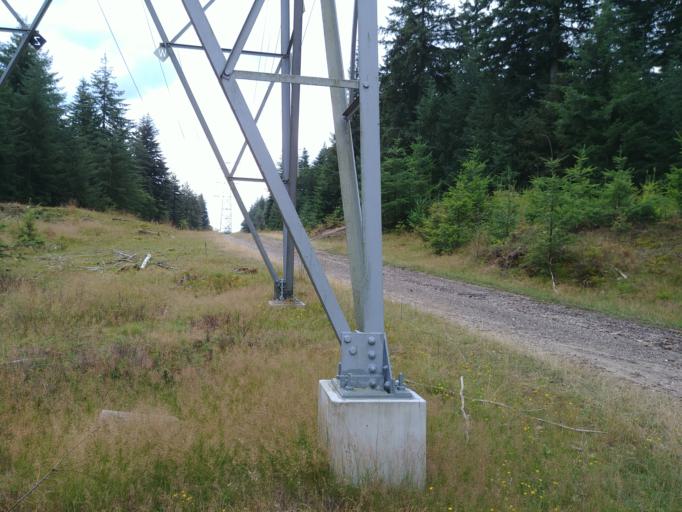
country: NL
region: Gelderland
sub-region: Gemeente Apeldoorn
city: Beekbergen
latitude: 52.1138
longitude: 5.9593
